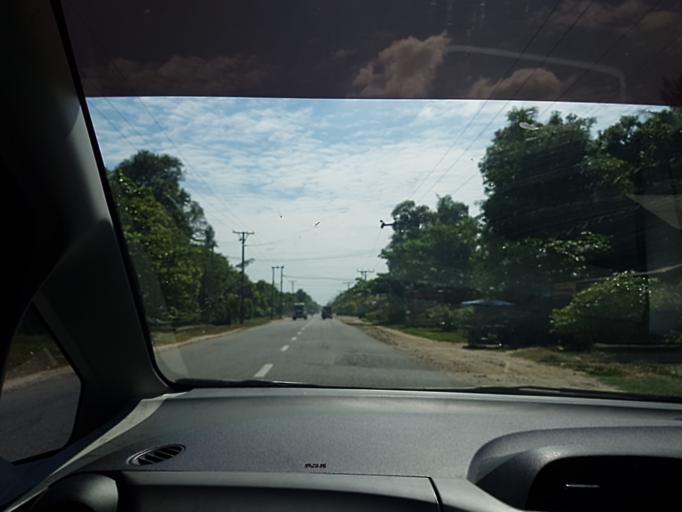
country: MM
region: Mon
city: Thaton
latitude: 16.7027
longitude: 97.4235
